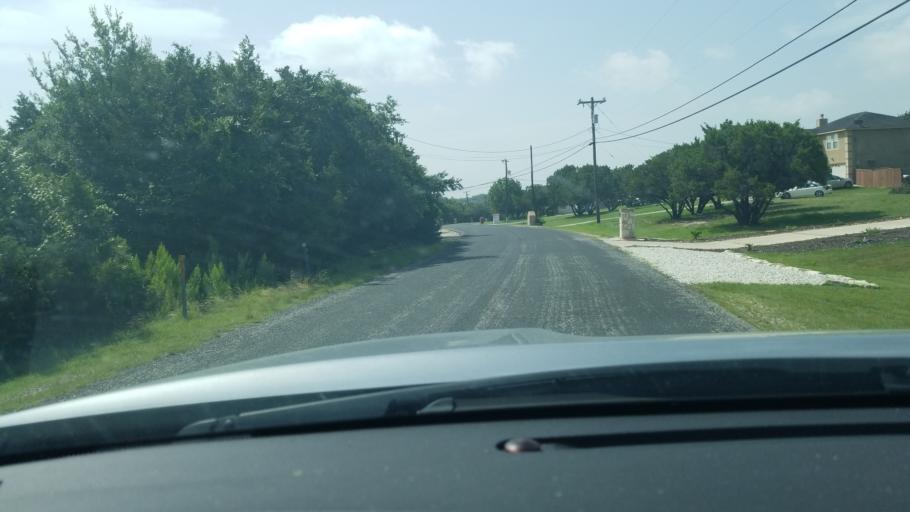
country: US
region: Texas
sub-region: Bexar County
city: Timberwood Park
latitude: 29.7036
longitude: -98.4933
